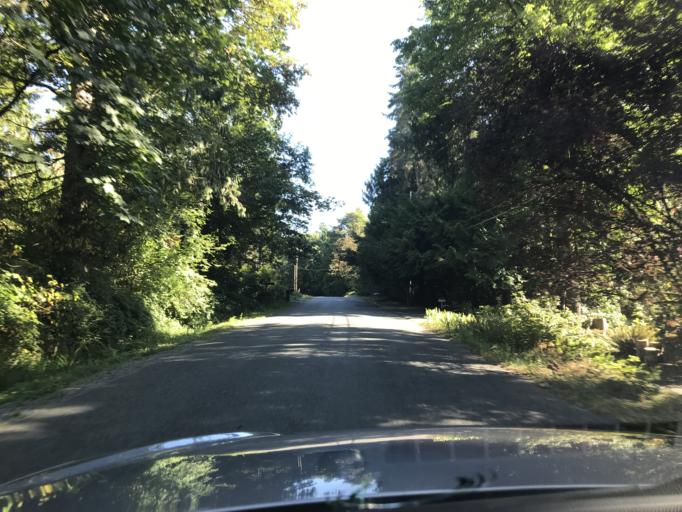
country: US
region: Washington
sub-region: King County
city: Maple Heights-Lake Desire
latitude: 47.4405
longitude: -122.0823
